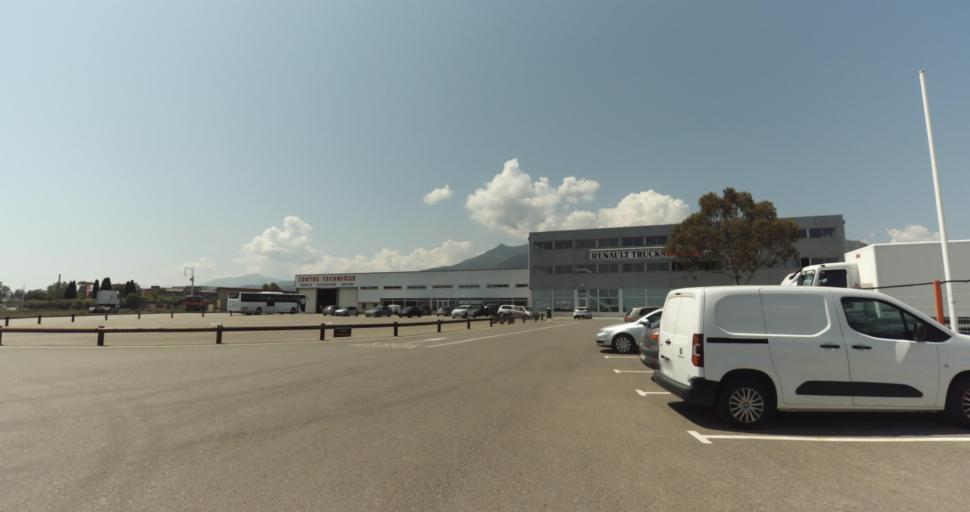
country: FR
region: Corsica
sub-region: Departement de la Haute-Corse
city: Biguglia
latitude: 42.6050
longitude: 9.4377
